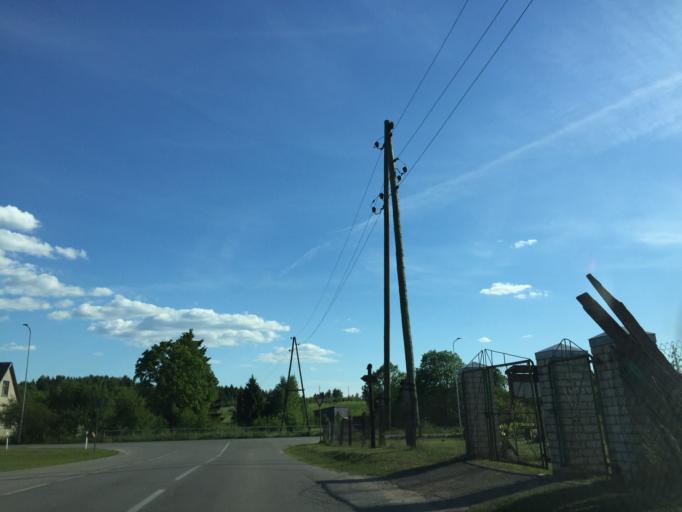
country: LV
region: Rezekne
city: Rezekne
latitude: 56.3438
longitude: 27.1668
